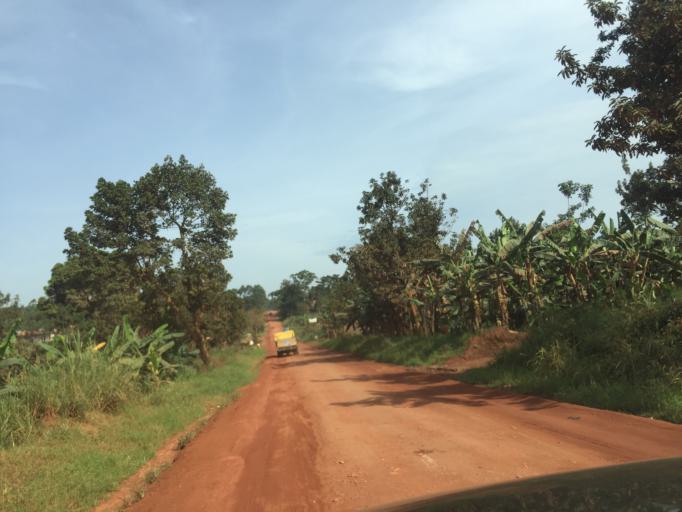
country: UG
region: Central Region
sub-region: Wakiso District
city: Wakiso
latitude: 0.4553
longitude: 32.5649
